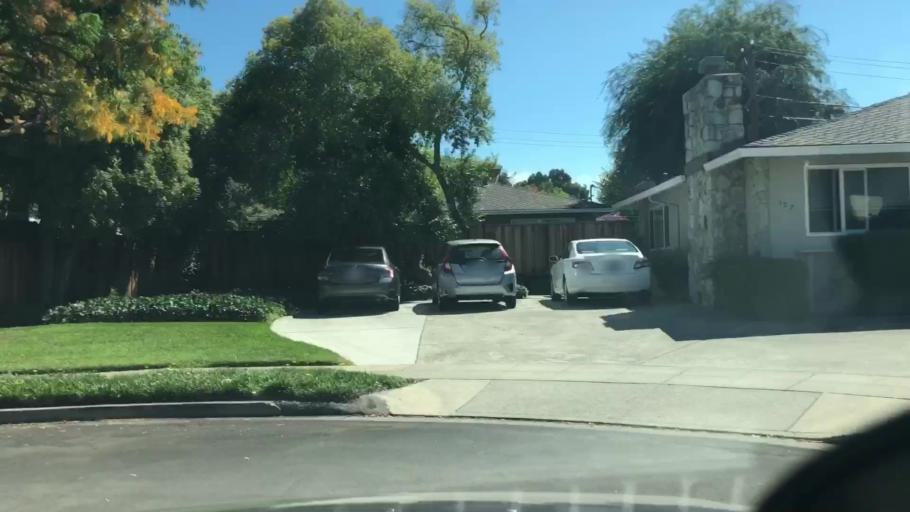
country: US
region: California
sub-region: Santa Clara County
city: Campbell
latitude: 37.2842
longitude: -121.9813
